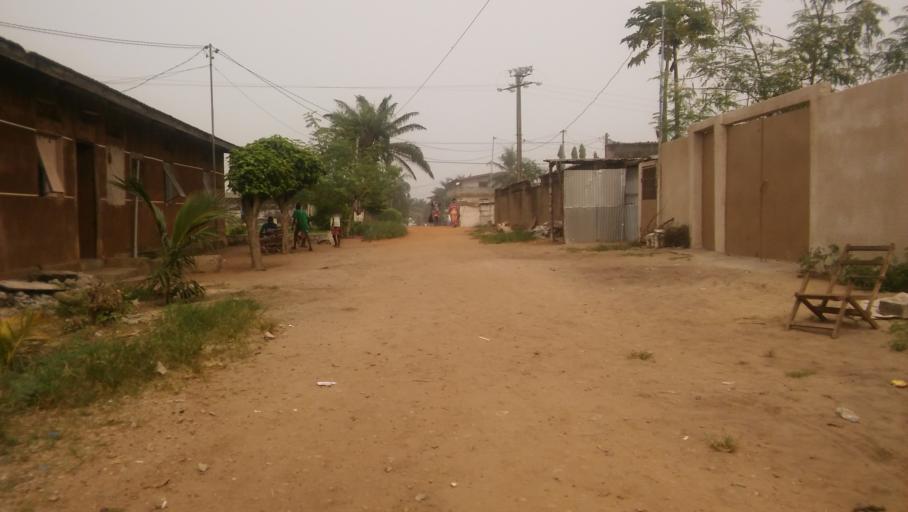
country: CI
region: Sud-Comoe
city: Grand-Bassam
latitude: 5.2182
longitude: -3.7307
